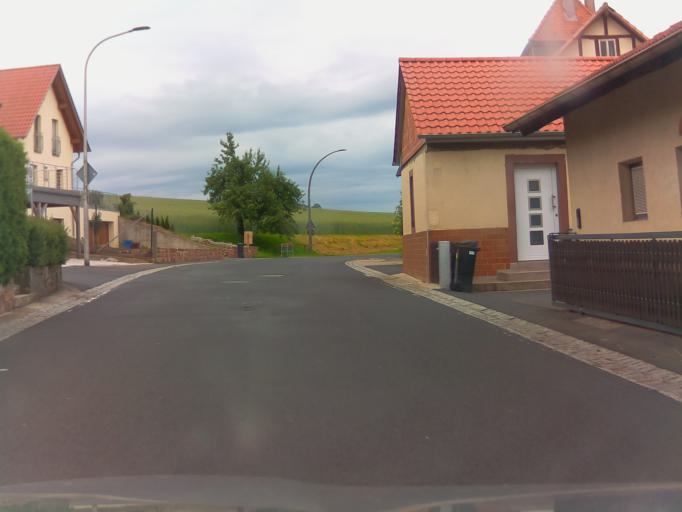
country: DE
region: Bavaria
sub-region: Regierungsbezirk Unterfranken
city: Wartmannsroth
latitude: 50.1447
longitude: 9.7784
